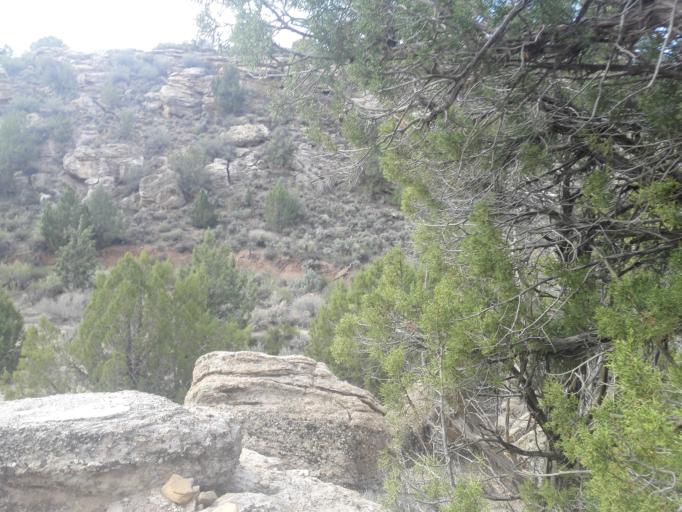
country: US
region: Colorado
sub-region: Montezuma County
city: Towaoc
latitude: 37.3828
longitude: -109.0745
